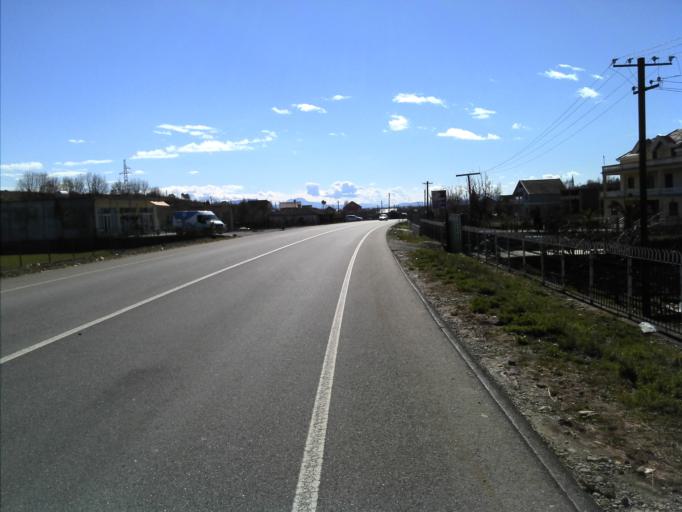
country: AL
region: Shkoder
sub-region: Rrethi i Malesia e Madhe
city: Koplik
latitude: 42.1871
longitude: 19.4582
